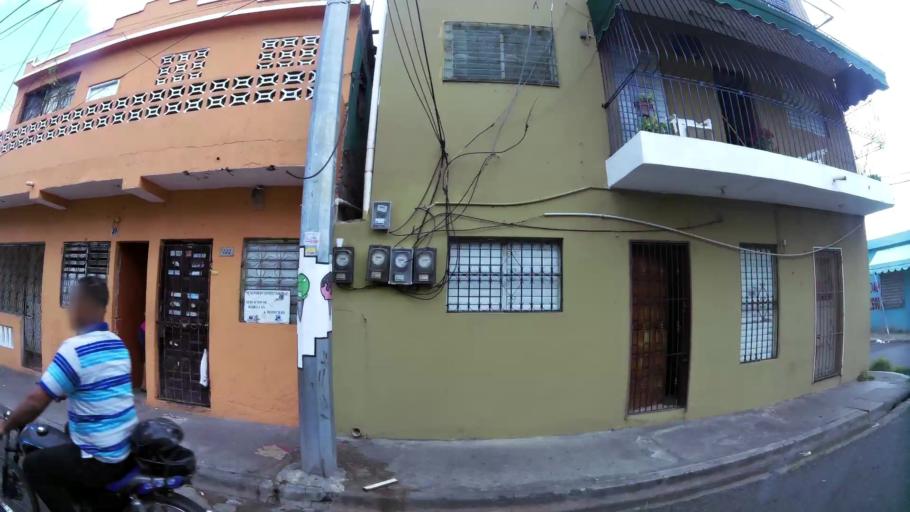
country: DO
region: Nacional
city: San Carlos
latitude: 18.4820
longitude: -69.8992
